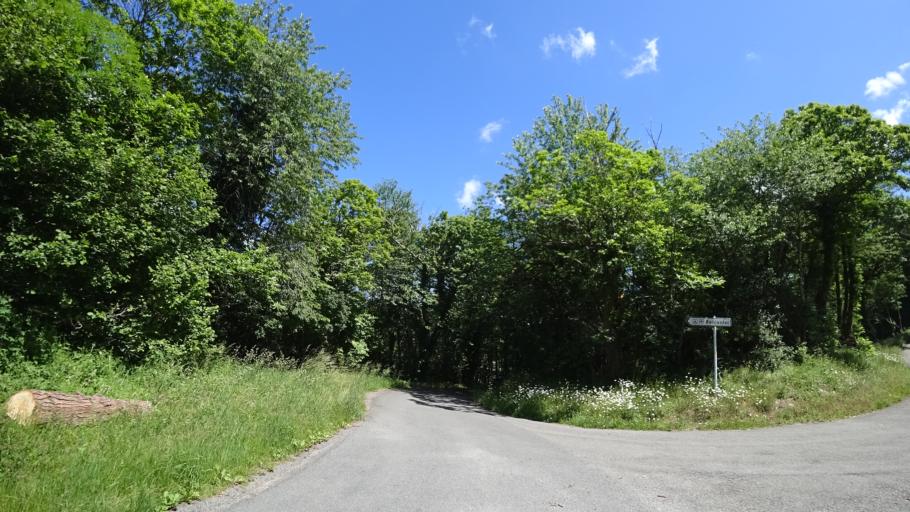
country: FR
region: Midi-Pyrenees
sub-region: Departement de l'Aveyron
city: Colombies
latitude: 44.3846
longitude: 2.3337
